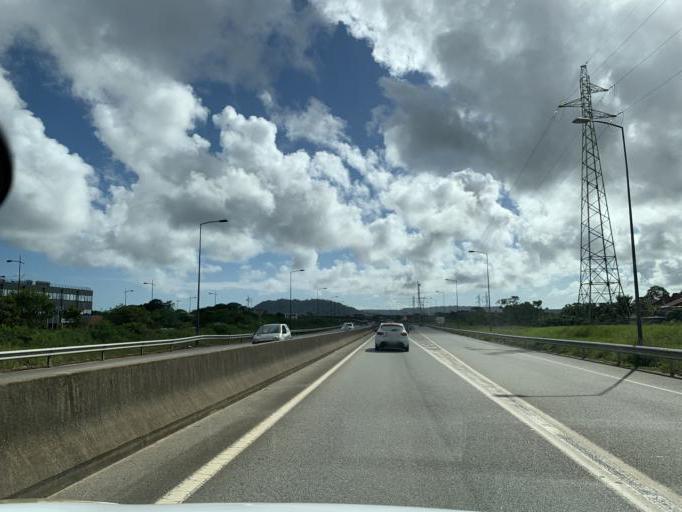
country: GF
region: Guyane
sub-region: Guyane
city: Cayenne
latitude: 4.8912
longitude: -52.3381
